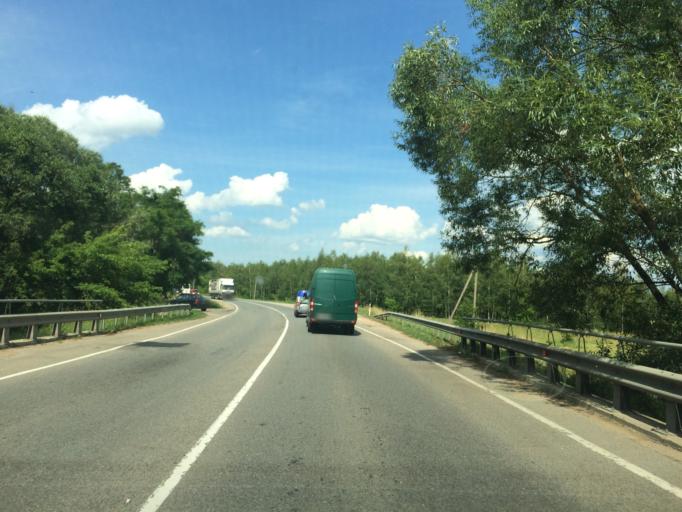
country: LT
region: Kauno apskritis
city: Jonava
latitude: 55.0692
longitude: 24.2925
